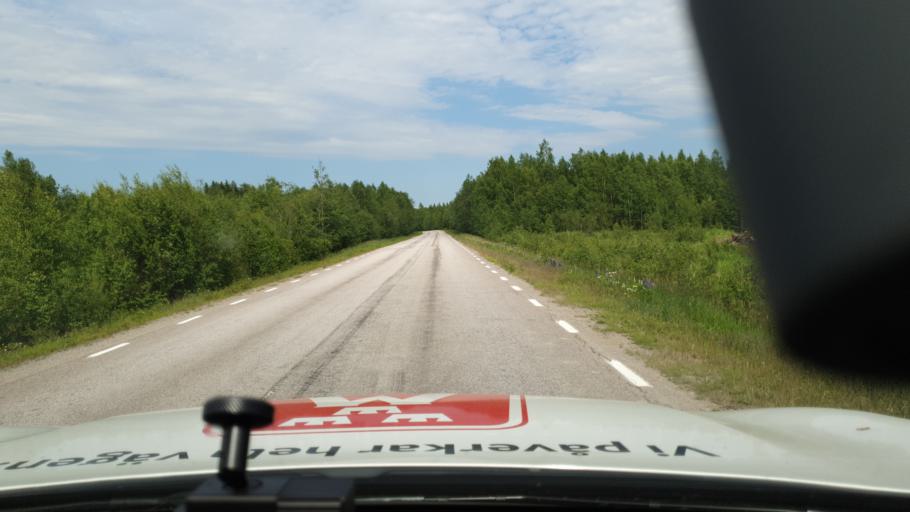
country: SE
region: Vaesterbotten
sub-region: Umea Kommun
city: Hoernefors
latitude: 63.5978
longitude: 19.8506
